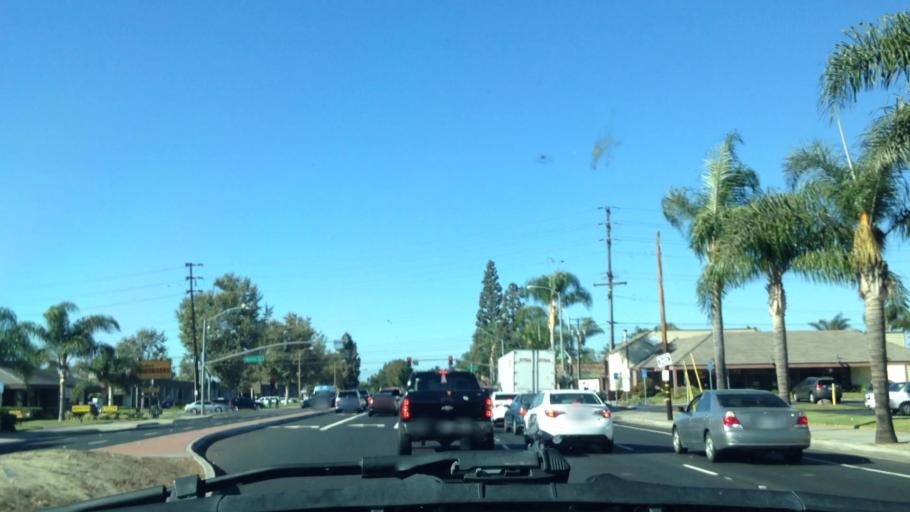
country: US
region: California
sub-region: Orange County
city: Fountain Valley
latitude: 33.7141
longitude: -117.9078
